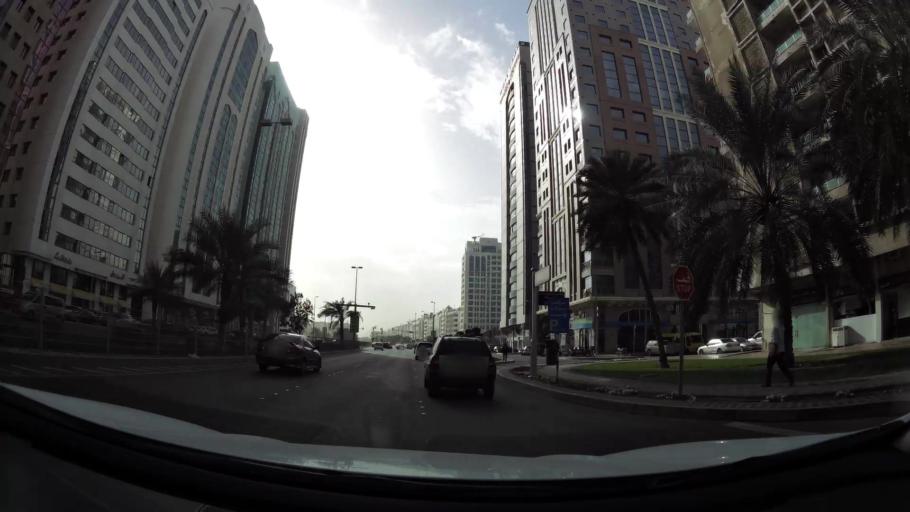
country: AE
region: Abu Dhabi
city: Abu Dhabi
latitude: 24.4846
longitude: 54.3745
